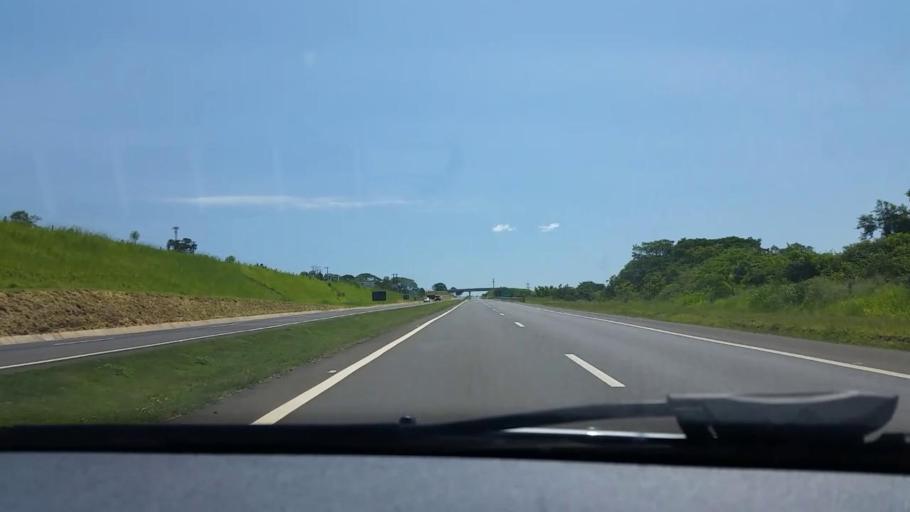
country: BR
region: Sao Paulo
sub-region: Bauru
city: Bauru
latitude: -22.4044
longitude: -49.0947
